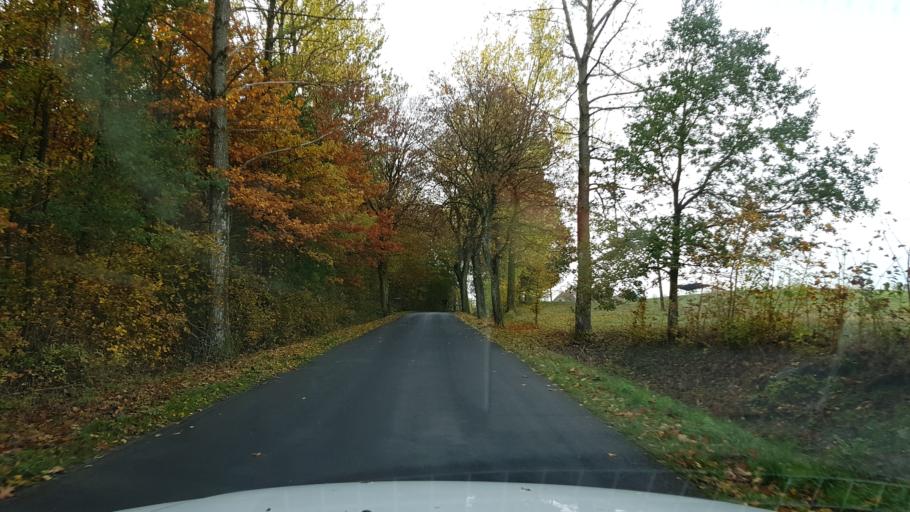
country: PL
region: West Pomeranian Voivodeship
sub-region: Powiat swidwinski
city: Polczyn-Zdroj
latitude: 53.7479
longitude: 16.0478
